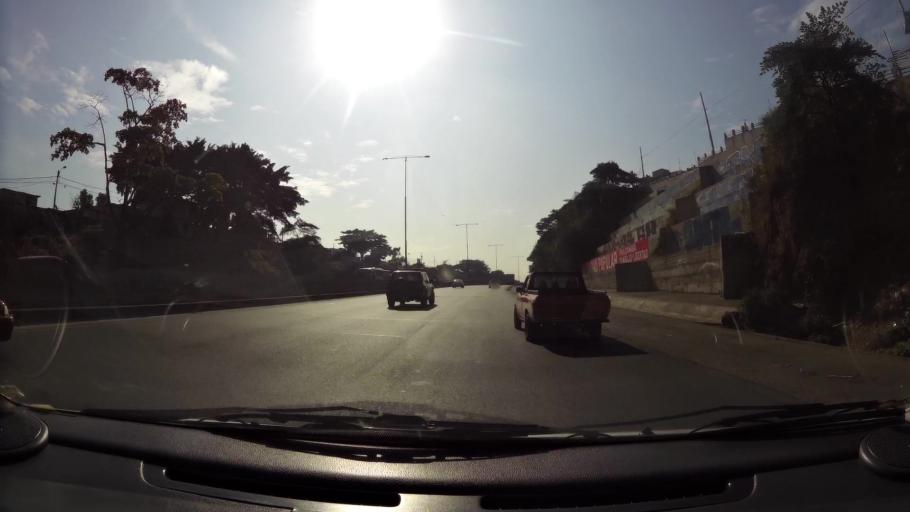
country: EC
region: Guayas
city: Santa Lucia
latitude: -2.0796
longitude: -79.9335
